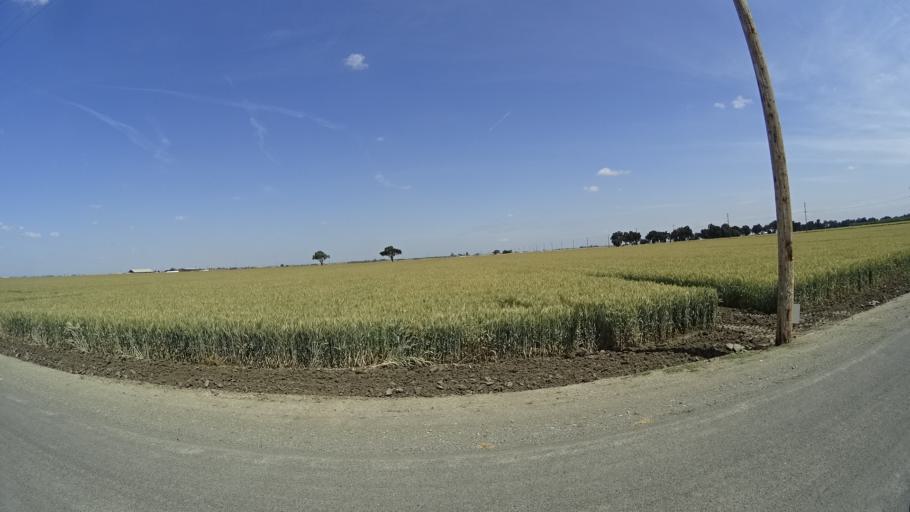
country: US
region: California
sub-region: Tulare County
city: Goshen
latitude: 36.2833
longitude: -119.4766
